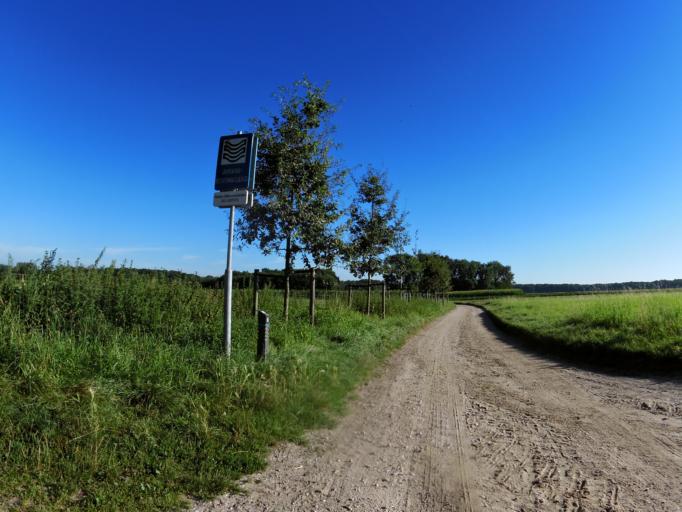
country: NL
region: Limburg
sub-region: Gemeente Onderbanken
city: Schinveld
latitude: 50.9651
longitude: 5.9936
